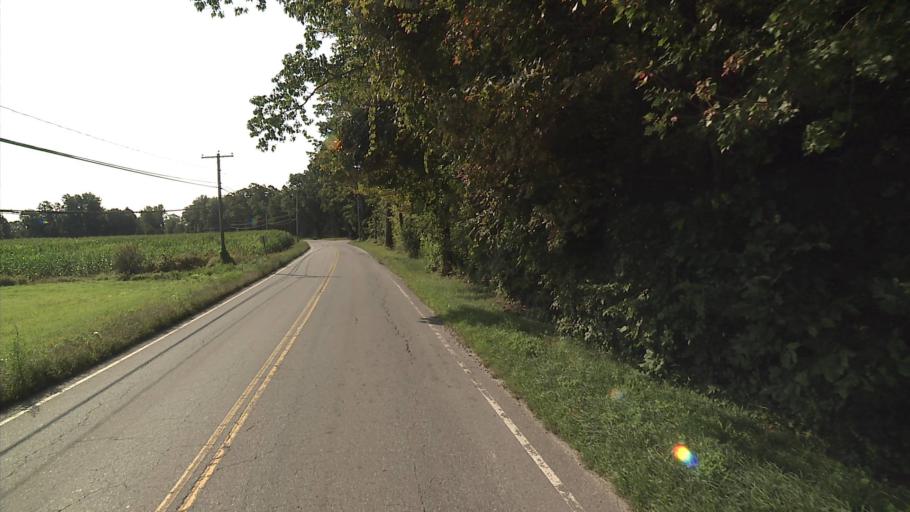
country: US
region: Connecticut
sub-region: Windham County
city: South Windham
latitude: 41.6200
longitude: -72.1978
